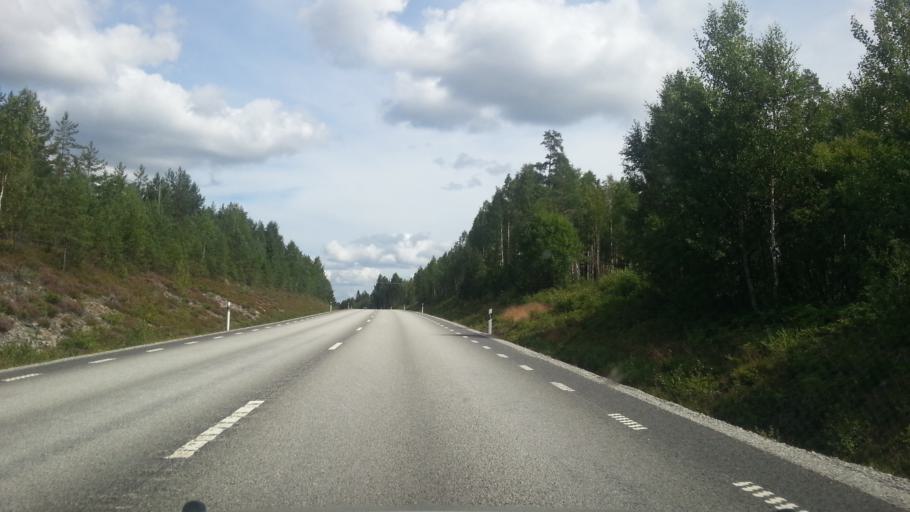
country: SE
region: Vaestmanland
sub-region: Skinnskattebergs Kommun
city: Skinnskatteberg
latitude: 59.7610
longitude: 15.4734
